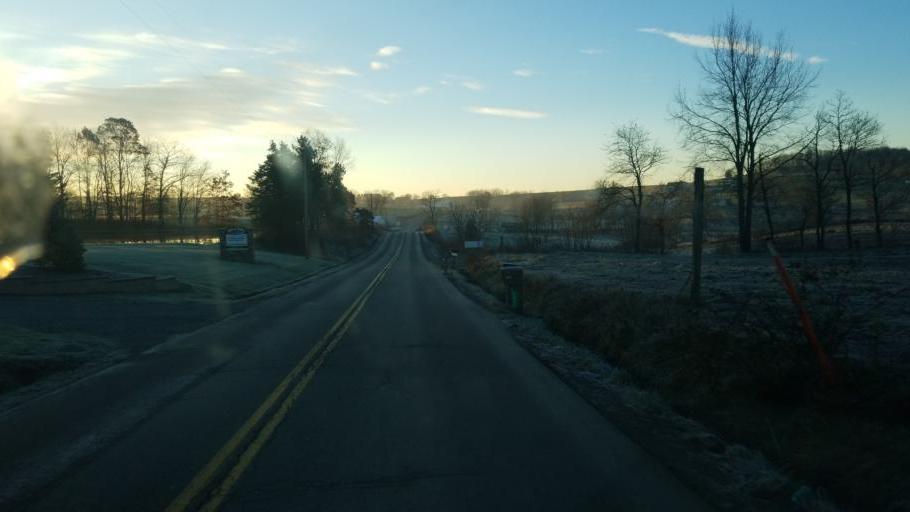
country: US
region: Ohio
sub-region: Wayne County
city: Apple Creek
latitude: 40.6501
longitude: -81.8536
